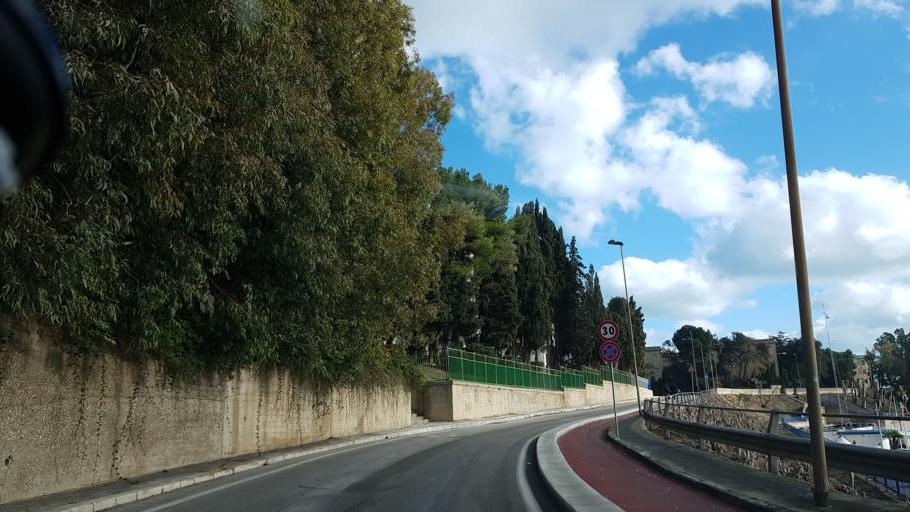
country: IT
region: Apulia
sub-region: Provincia di Brindisi
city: Brindisi
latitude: 40.6440
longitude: 17.9360
